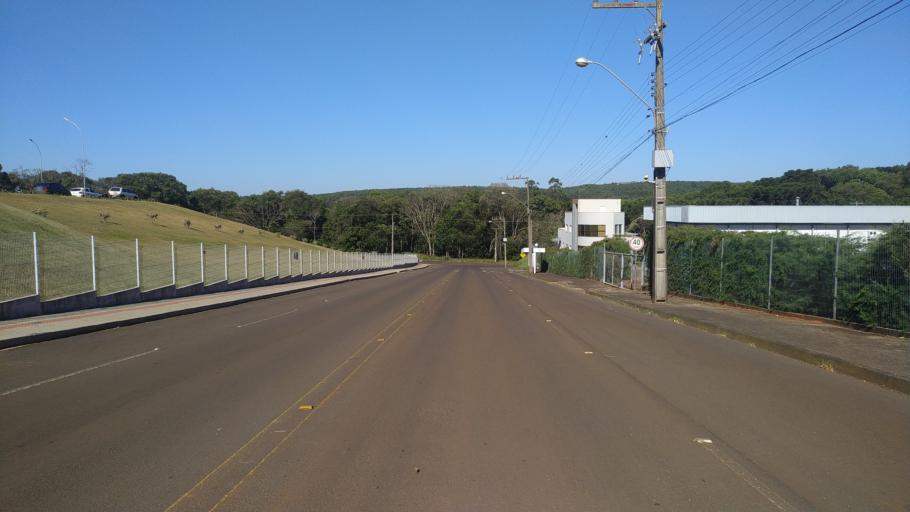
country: BR
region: Santa Catarina
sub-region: Chapeco
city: Chapeco
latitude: -27.1596
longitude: -52.6029
